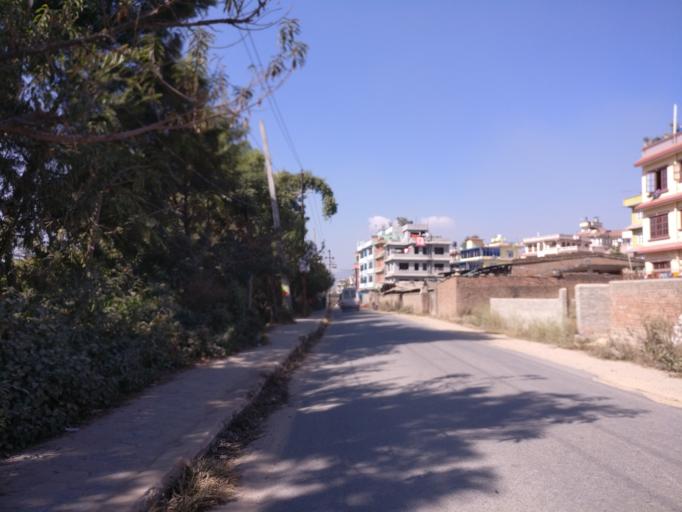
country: NP
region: Central Region
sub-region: Bagmati Zone
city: Patan
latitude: 27.6746
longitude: 85.3404
